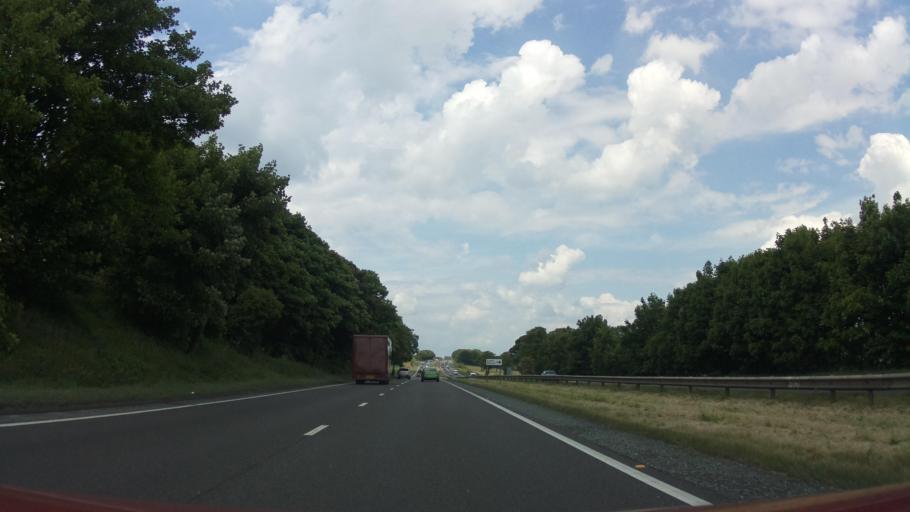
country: GB
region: England
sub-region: North Yorkshire
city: Thirsk
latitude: 54.3062
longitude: -1.3371
